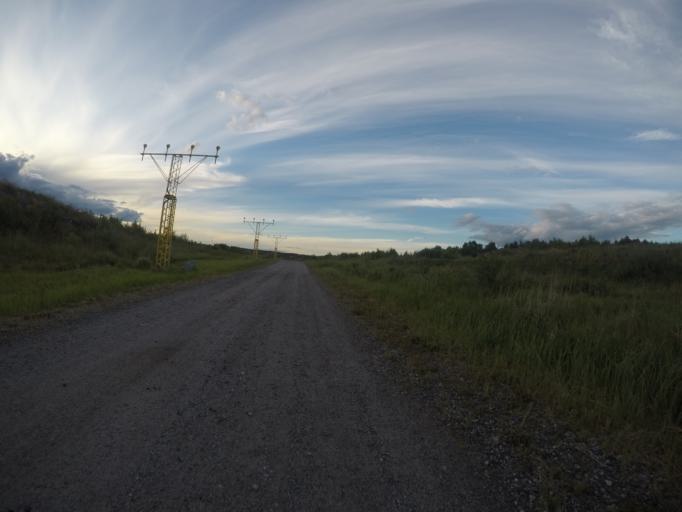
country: SE
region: Stockholm
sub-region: Sigtuna Kommun
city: Rosersberg
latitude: 59.6557
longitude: 17.9615
